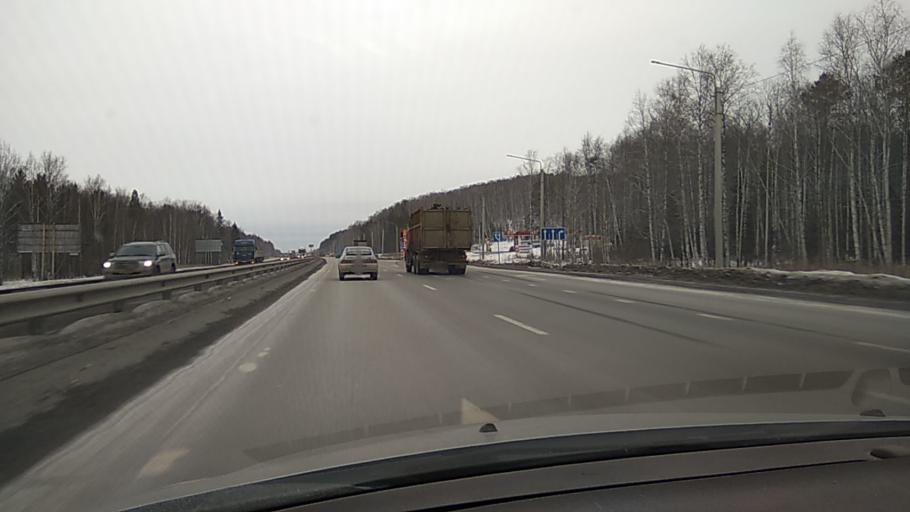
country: RU
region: Sverdlovsk
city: Severka
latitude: 56.8441
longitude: 60.2102
